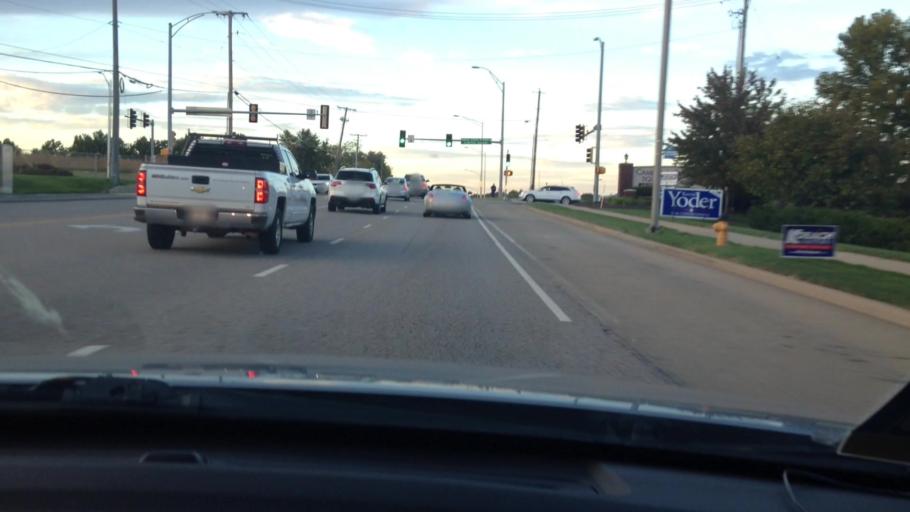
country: US
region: Kansas
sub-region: Johnson County
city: Leawood
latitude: 38.9342
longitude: -94.6488
